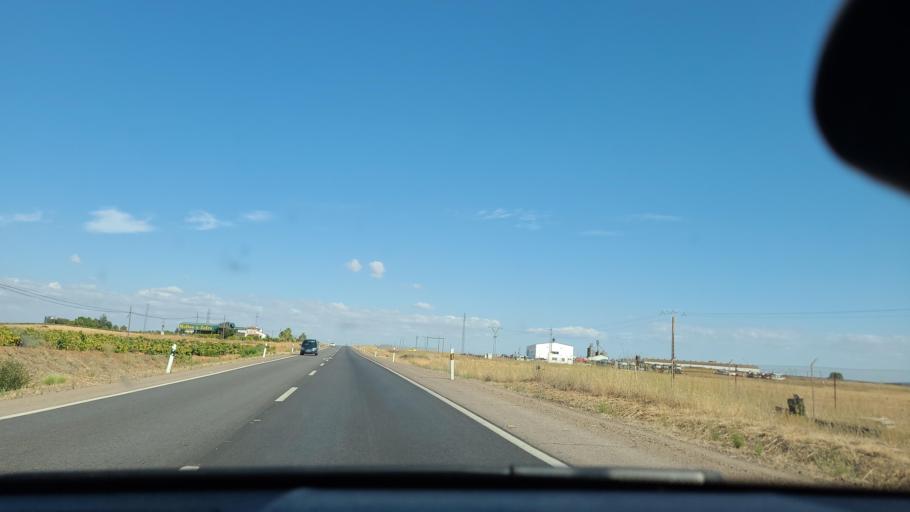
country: ES
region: Extremadura
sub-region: Provincia de Badajoz
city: Puebla de Sancho Perez
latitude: 38.4120
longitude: -6.3935
